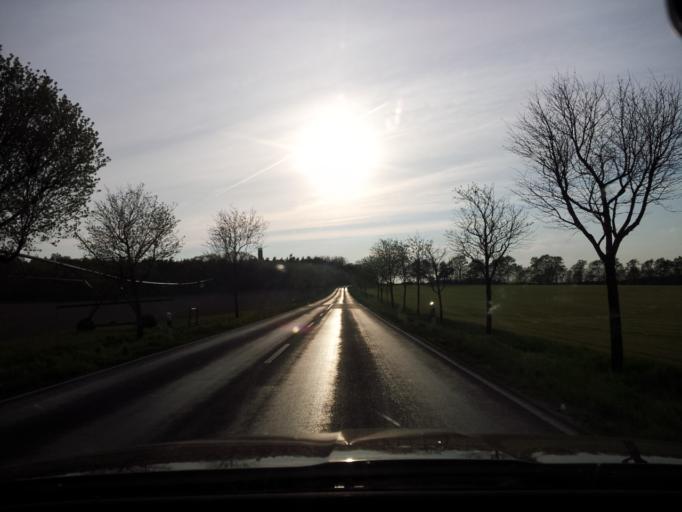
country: DE
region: Brandenburg
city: Dahme
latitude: 51.8521
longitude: 13.5098
